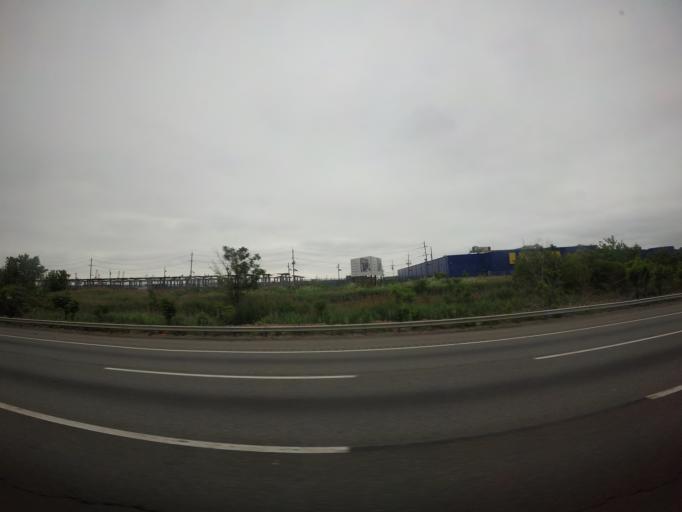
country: US
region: New Jersey
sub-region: Union County
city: Elizabeth
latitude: 40.6776
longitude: -74.1707
